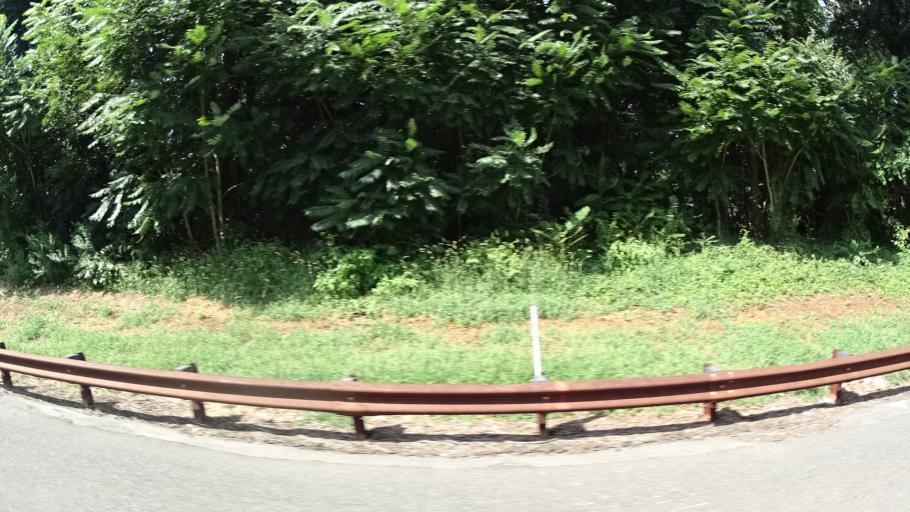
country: US
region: New Jersey
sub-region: Monmouth County
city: Tinton Falls
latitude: 40.3107
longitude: -74.0961
